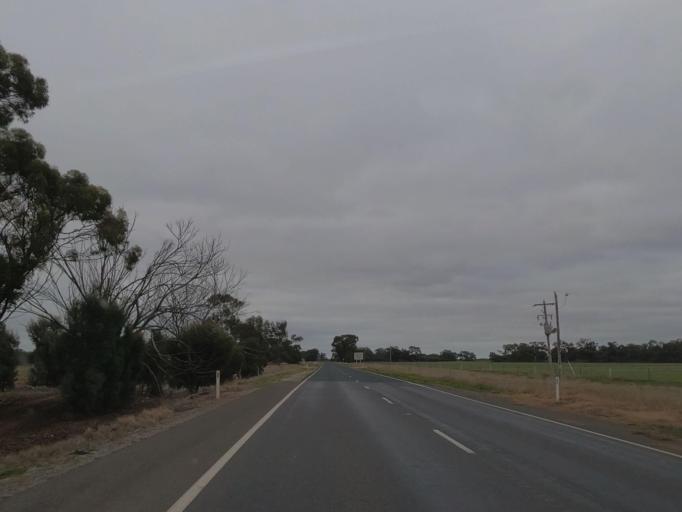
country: AU
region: Victoria
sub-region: Greater Bendigo
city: Long Gully
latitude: -36.1232
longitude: 143.9223
